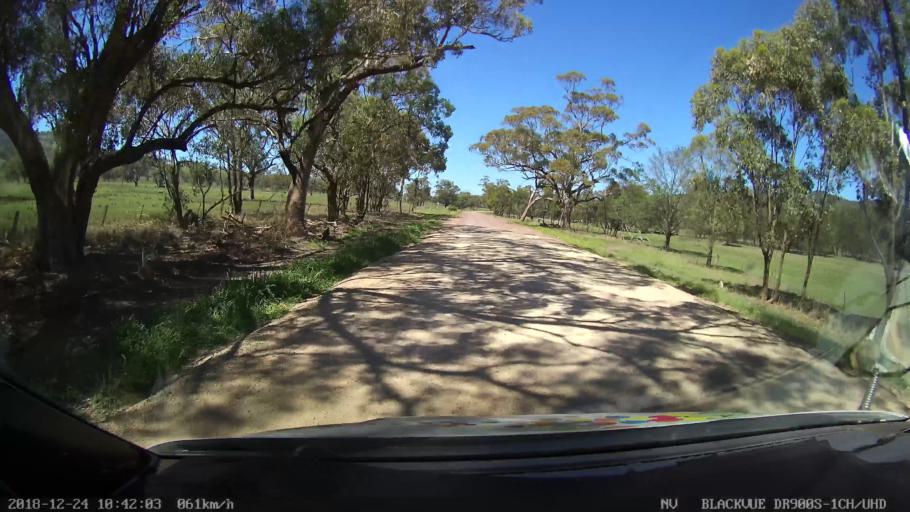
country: AU
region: New South Wales
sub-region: Upper Hunter Shire
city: Merriwa
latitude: -31.8736
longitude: 150.4554
